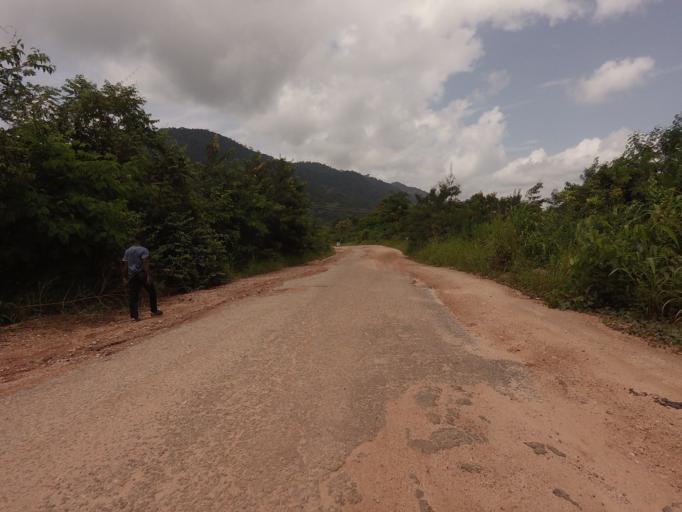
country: GH
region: Volta
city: Ho
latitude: 6.7681
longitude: 0.3639
